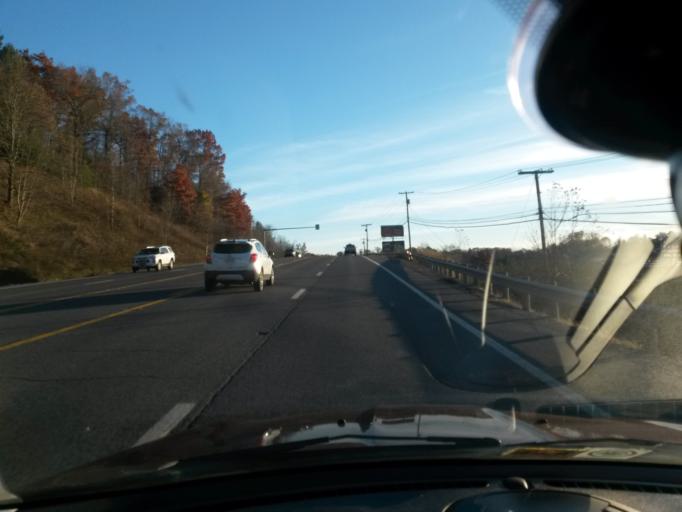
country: US
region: West Virginia
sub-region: Raleigh County
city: Prosperity
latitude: 37.8375
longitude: -81.1942
